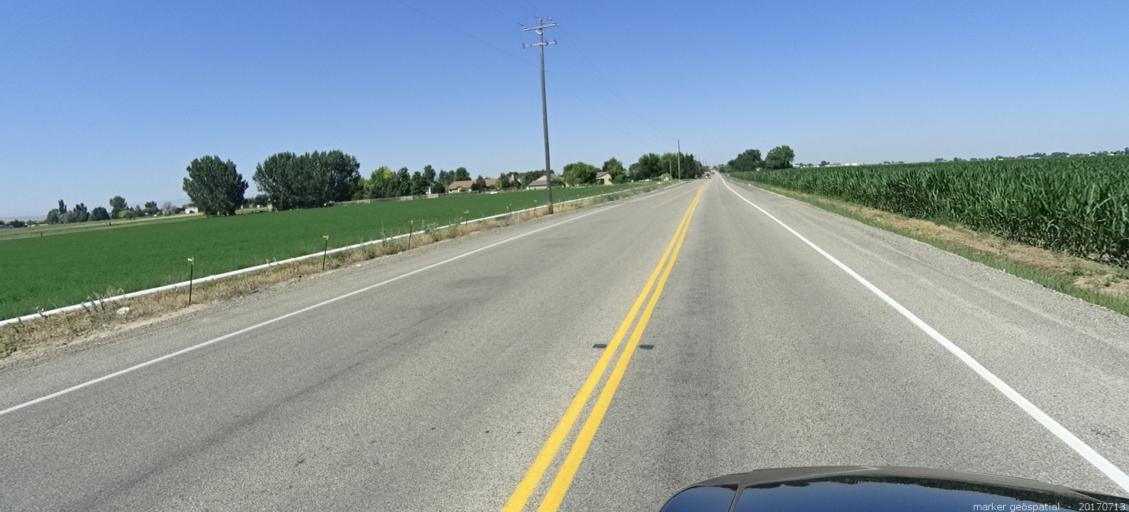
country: US
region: Idaho
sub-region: Ada County
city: Kuna
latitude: 43.5319
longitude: -116.3948
